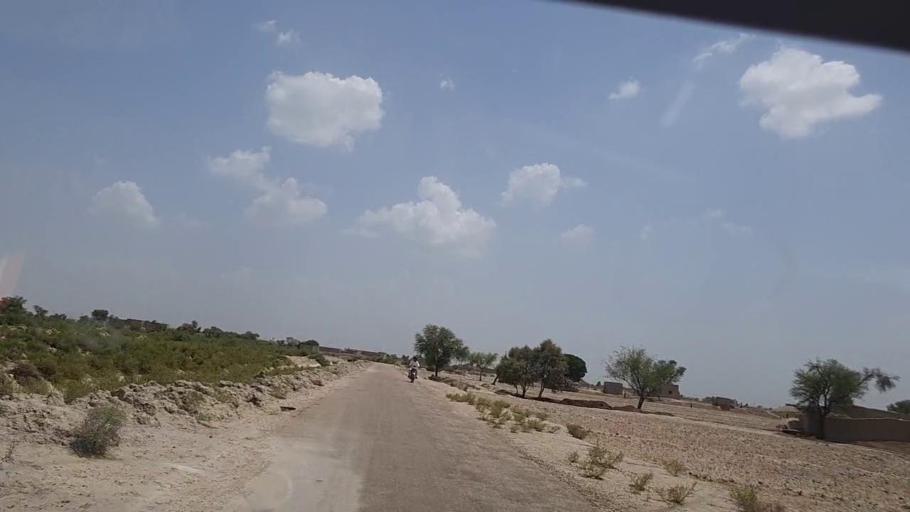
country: PK
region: Sindh
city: Bhan
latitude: 26.5240
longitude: 67.6346
